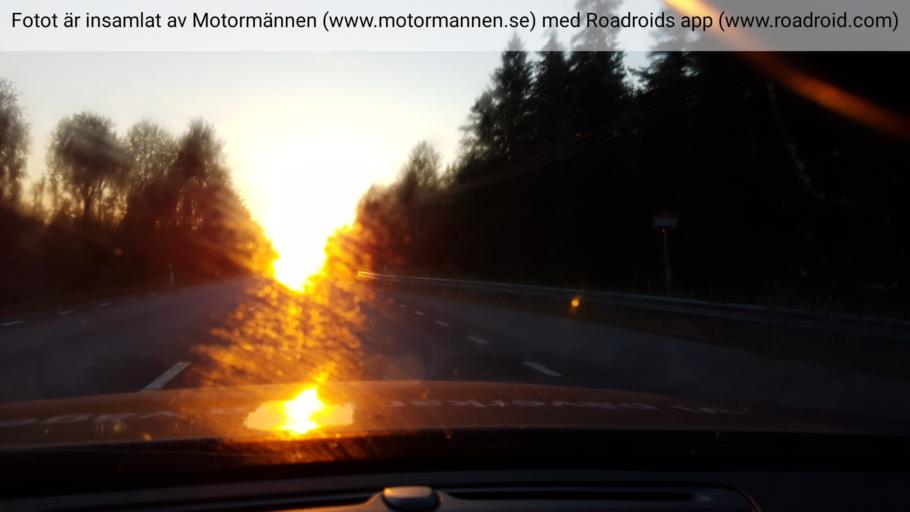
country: SE
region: Uppsala
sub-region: Osthammars Kommun
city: Bjorklinge
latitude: 59.9665
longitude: 17.3815
